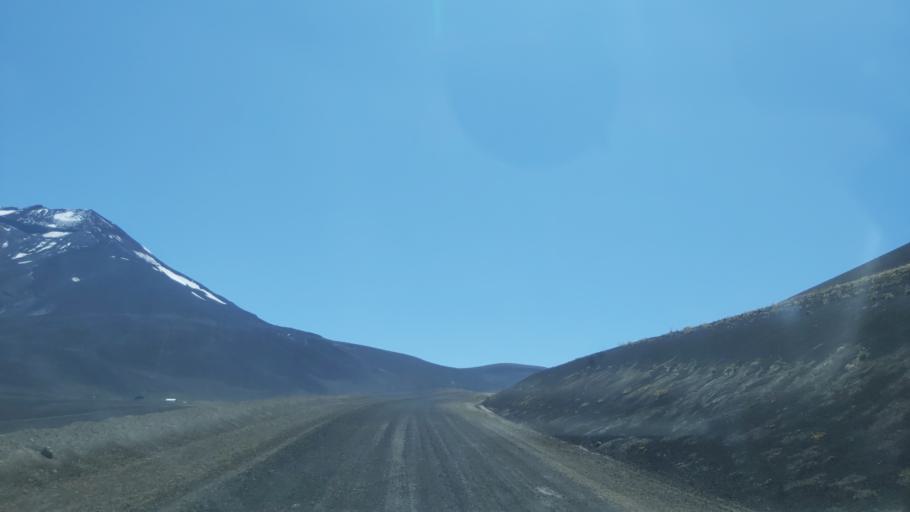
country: CL
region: Araucania
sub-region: Provincia de Cautin
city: Vilcun
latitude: -38.4058
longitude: -71.5433
